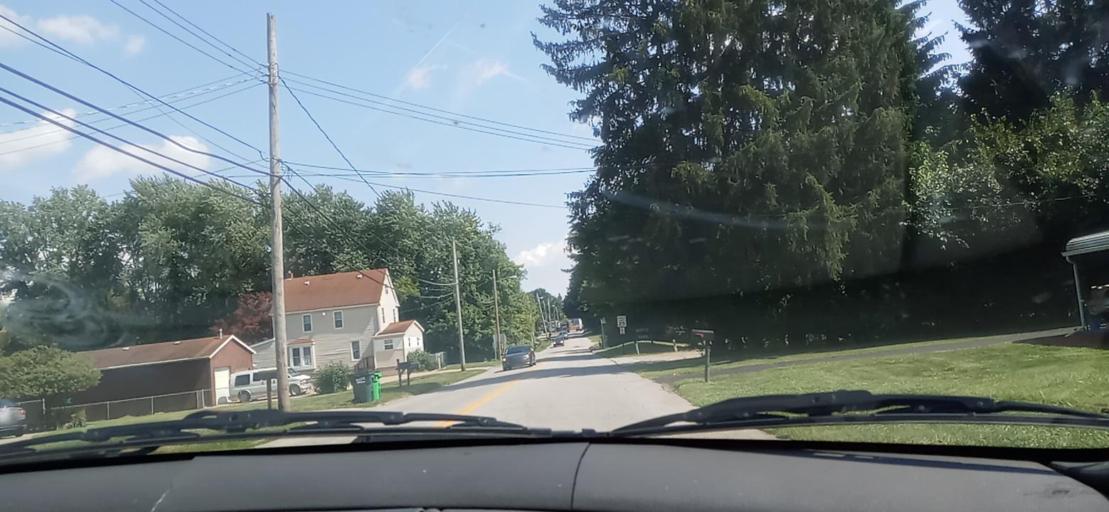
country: US
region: Ohio
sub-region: Summit County
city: Barberton
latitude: 41.0386
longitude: -81.5792
